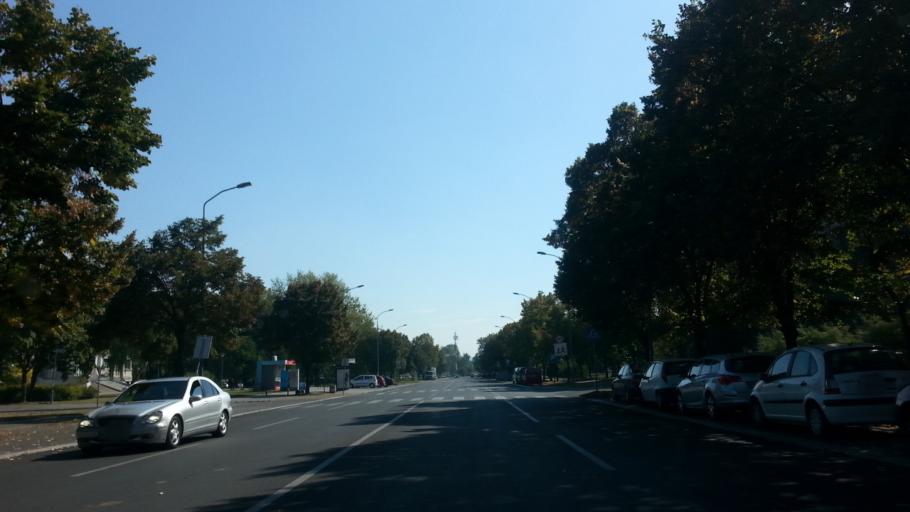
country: RS
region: Central Serbia
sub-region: Belgrade
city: Cukarica
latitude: 44.7997
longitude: 20.3822
